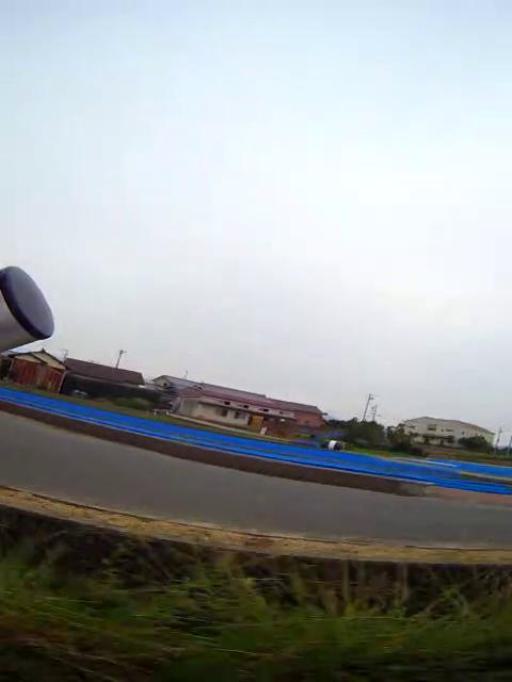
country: JP
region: Hyogo
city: Fukura
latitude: 34.3011
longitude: 134.7859
